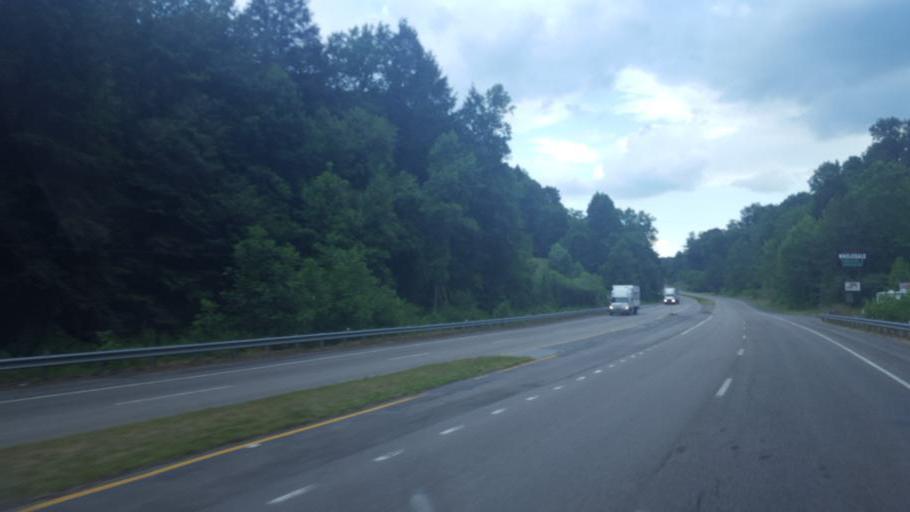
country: US
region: Virginia
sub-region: Wise County
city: Pound
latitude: 37.1360
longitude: -82.6234
